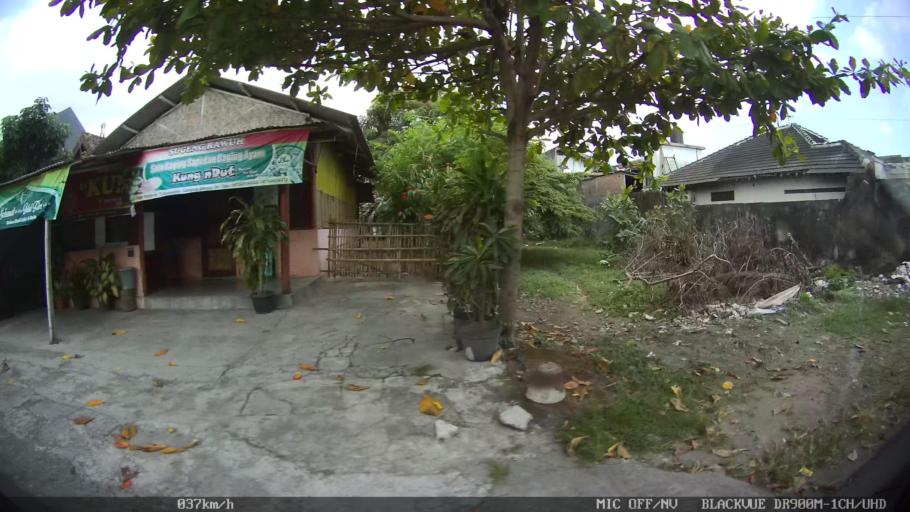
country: ID
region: Daerah Istimewa Yogyakarta
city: Gamping Lor
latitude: -7.7823
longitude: 110.3405
